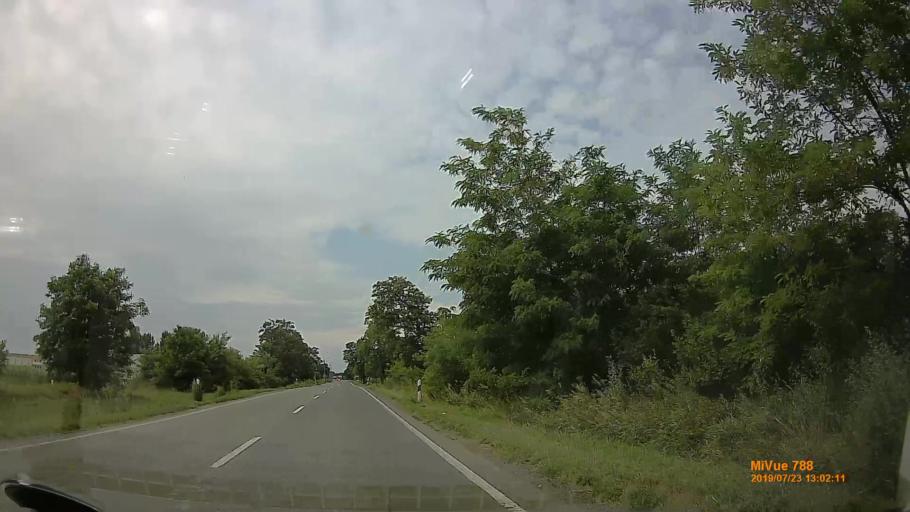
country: HU
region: Szabolcs-Szatmar-Bereg
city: Tiszavasvari
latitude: 47.9576
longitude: 21.3903
